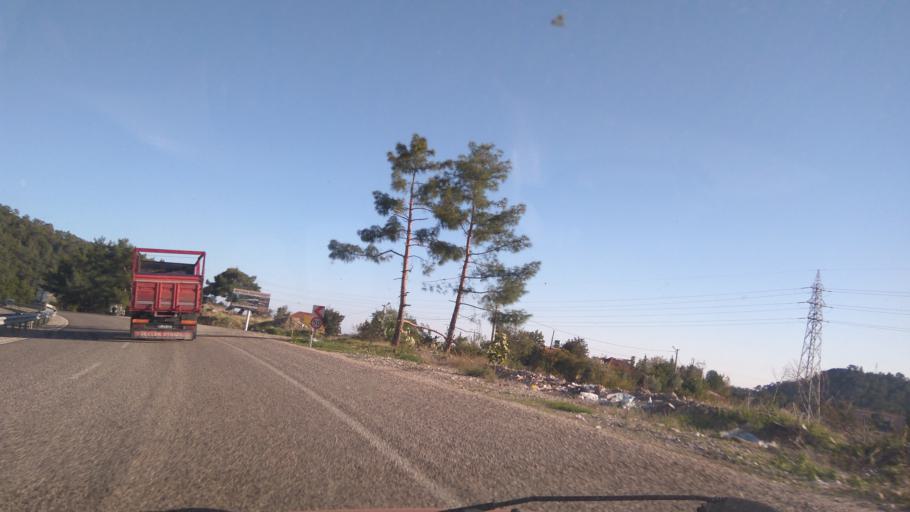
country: TR
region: Antalya
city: Kemer
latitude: 36.5826
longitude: 30.5453
